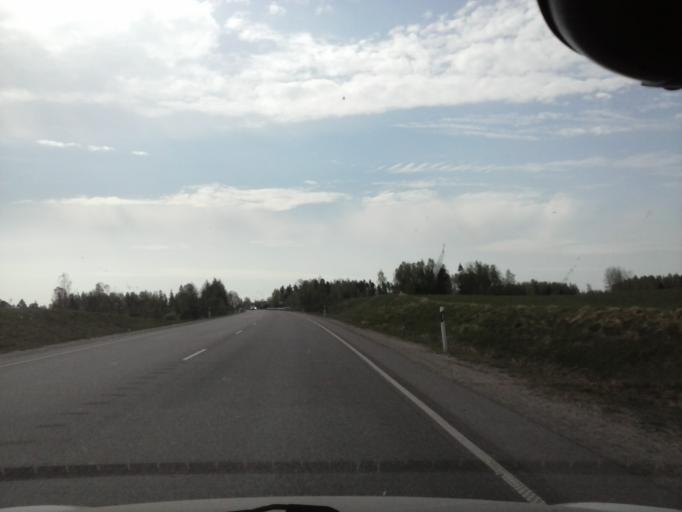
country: EE
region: Tartu
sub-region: UElenurme vald
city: Ulenurme
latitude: 58.1506
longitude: 26.6961
